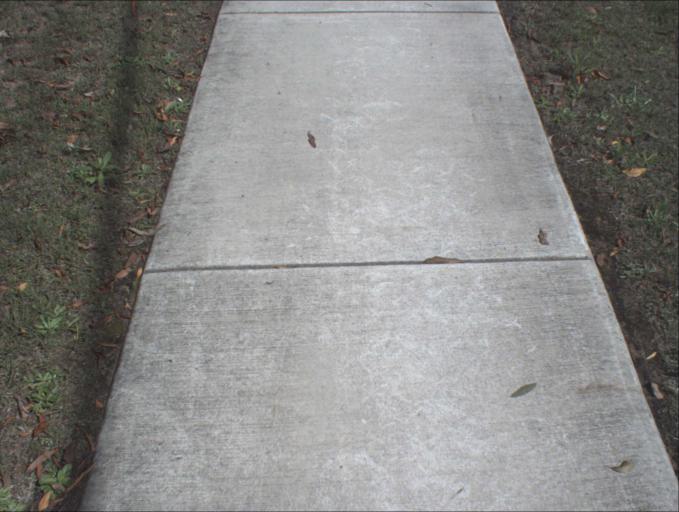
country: AU
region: Queensland
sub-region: Logan
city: Chambers Flat
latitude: -27.7460
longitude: 153.0540
